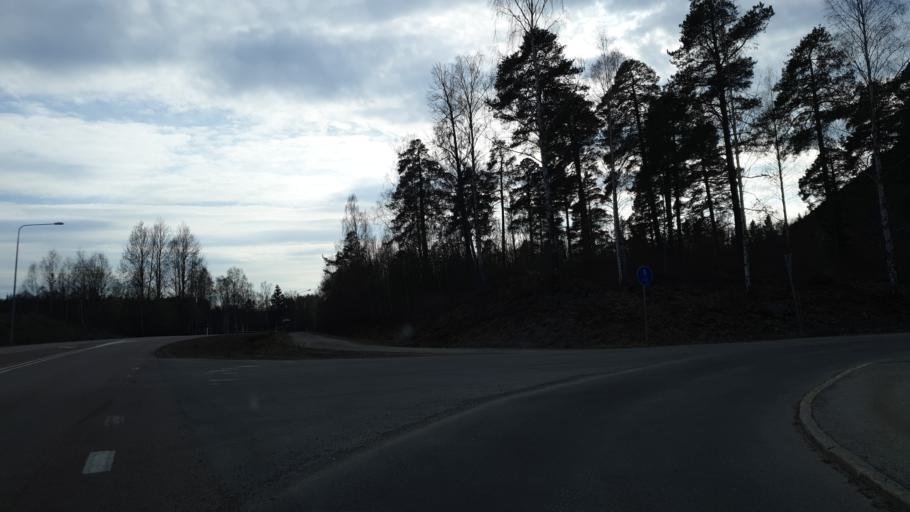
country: SE
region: Gaevleborg
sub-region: Hudiksvalls Kommun
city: Iggesund
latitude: 61.6374
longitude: 17.0770
